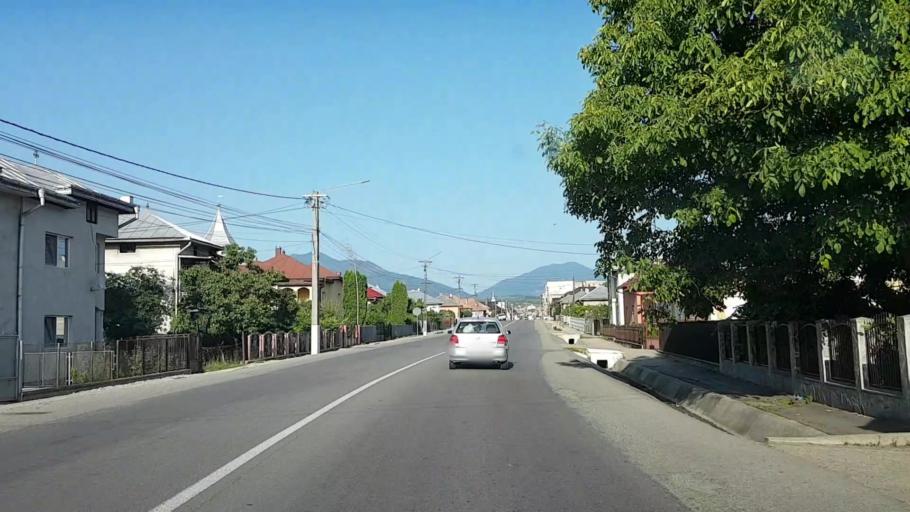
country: RO
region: Bistrita-Nasaud
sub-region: Comuna Prundu Bargaului
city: Susenii Bargaului
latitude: 47.2207
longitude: 24.7233
